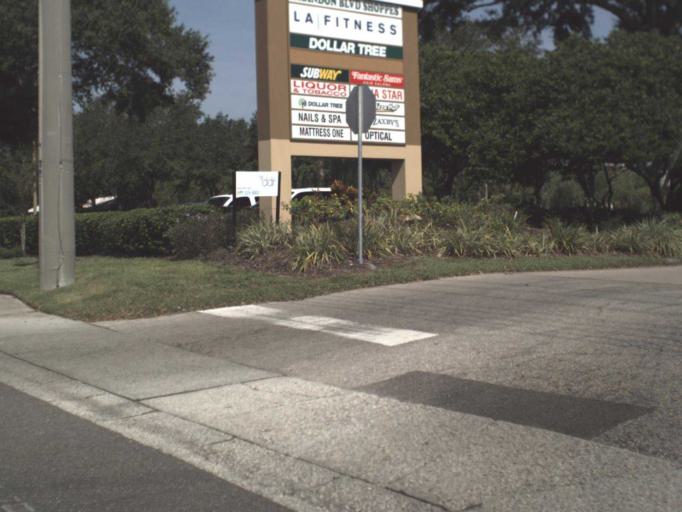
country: US
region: Florida
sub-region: Hillsborough County
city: Valrico
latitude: 27.9380
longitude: -82.2554
